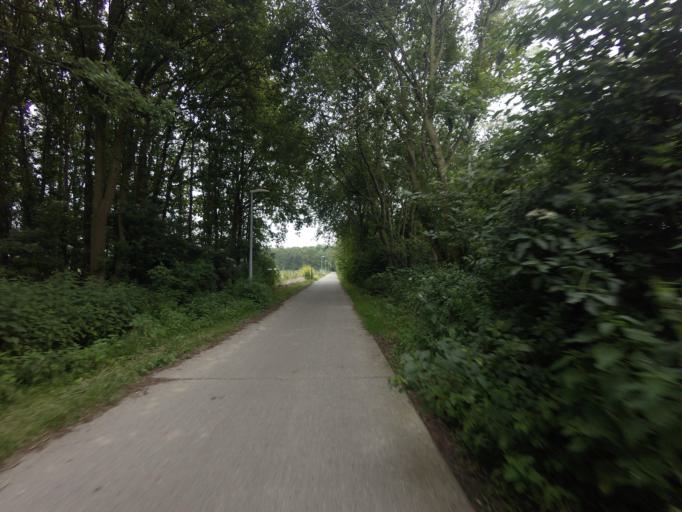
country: NL
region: Flevoland
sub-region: Gemeente Almere
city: Almere Stad
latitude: 52.3797
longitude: 5.2849
